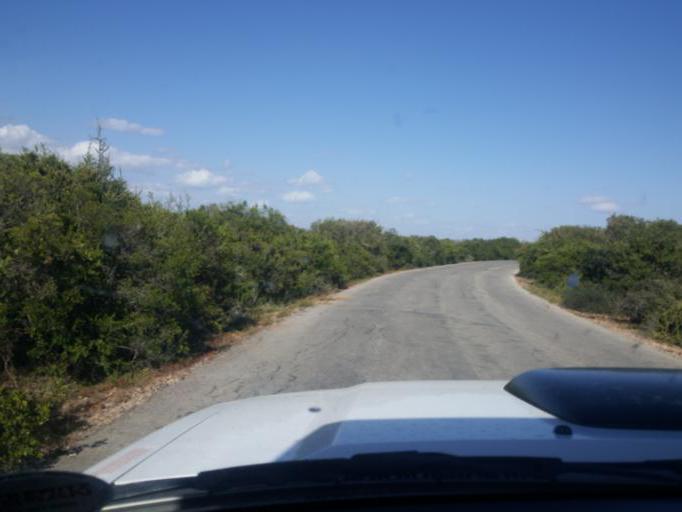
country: ZA
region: Eastern Cape
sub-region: Cacadu District Municipality
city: Kirkwood
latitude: -33.4411
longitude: 25.7611
